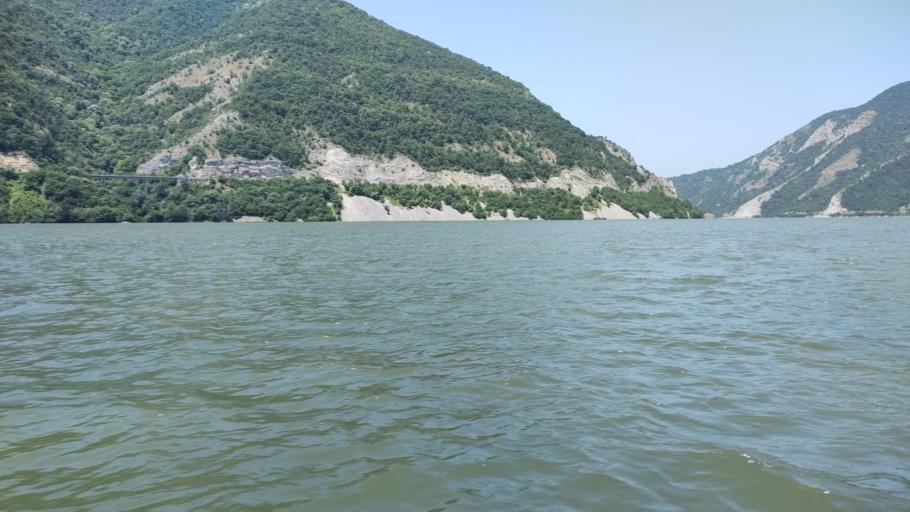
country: RO
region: Caras-Severin
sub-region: Comuna Berzasca
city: Berzasca
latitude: 44.5806
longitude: 22.0281
